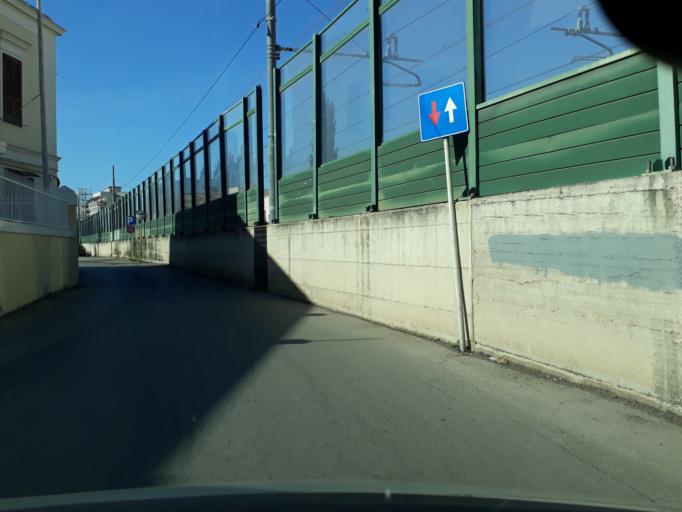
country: IT
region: Apulia
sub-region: Provincia di Bari
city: Monopoli
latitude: 40.9485
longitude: 17.2988
